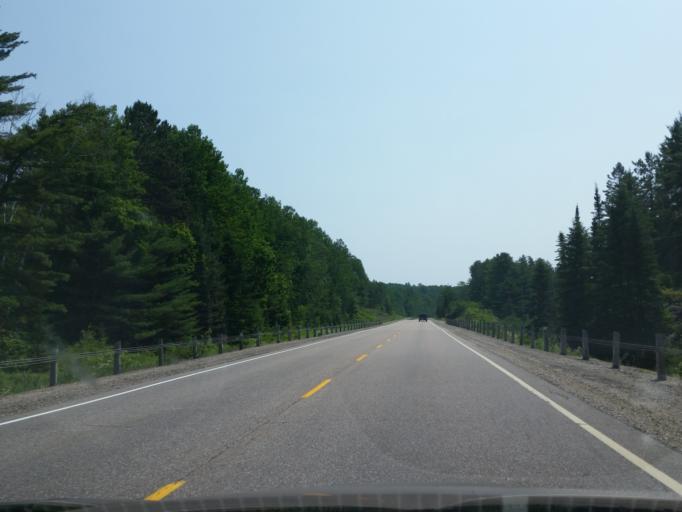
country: CA
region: Ontario
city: Deep River
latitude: 46.1818
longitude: -77.7348
